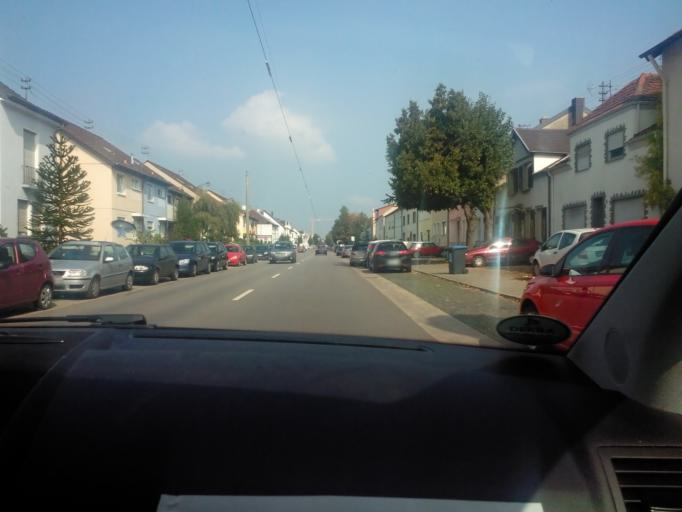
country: DE
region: Saarland
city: Saarlouis
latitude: 49.3031
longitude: 6.7585
